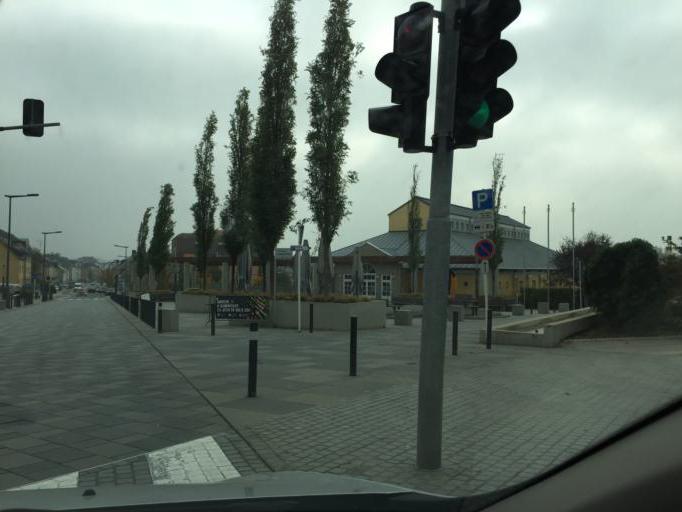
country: LU
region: Luxembourg
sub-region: Canton de Luxembourg
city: Sandweiler
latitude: 49.6165
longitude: 6.2184
